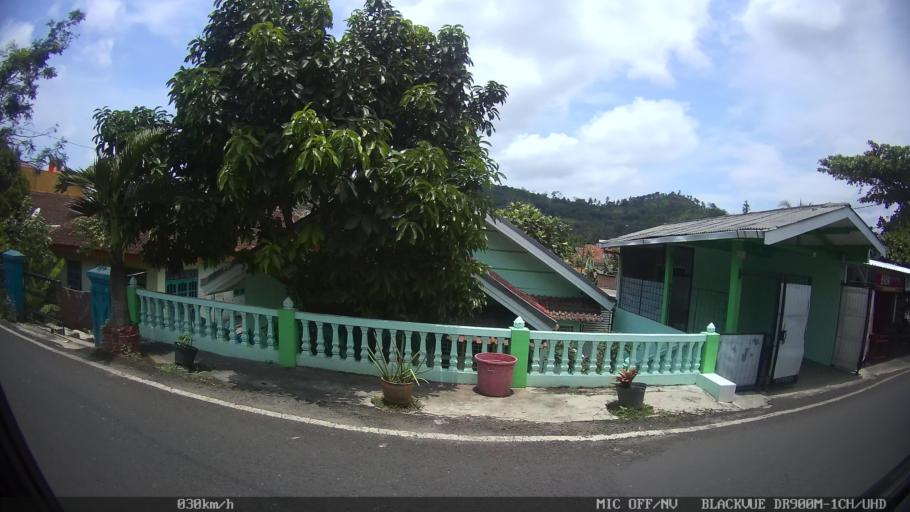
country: ID
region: Lampung
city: Bandarlampung
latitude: -5.4117
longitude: 105.2420
